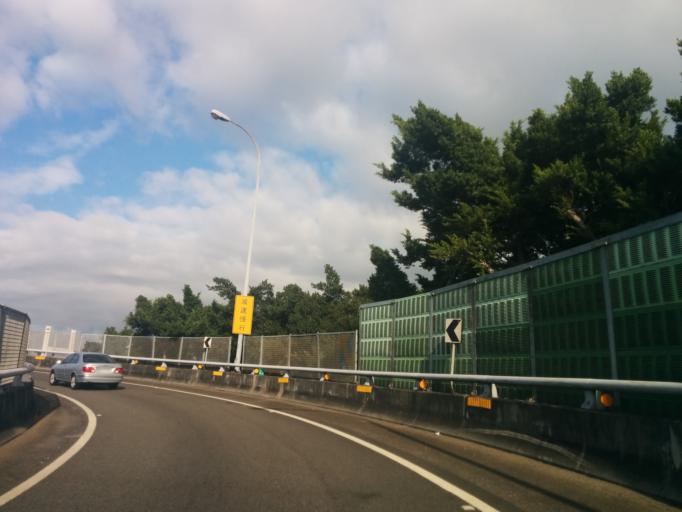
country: TW
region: Taipei
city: Taipei
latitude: 25.0821
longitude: 121.5081
